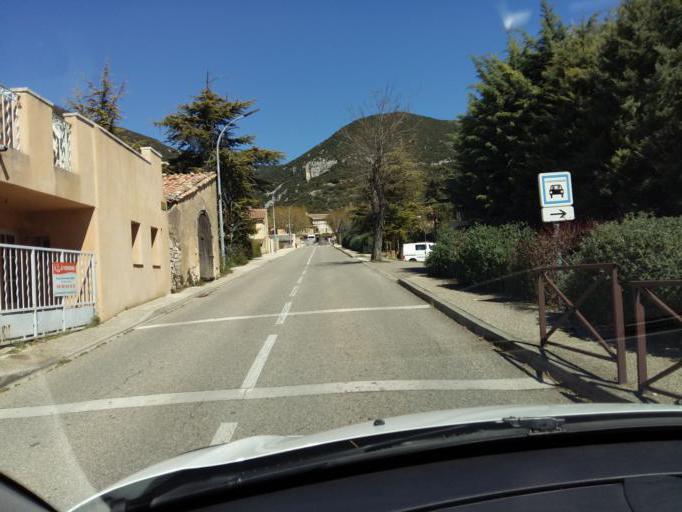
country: FR
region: Provence-Alpes-Cote d'Azur
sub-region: Departement du Vaucluse
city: Saignon
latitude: 43.9231
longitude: 5.4834
